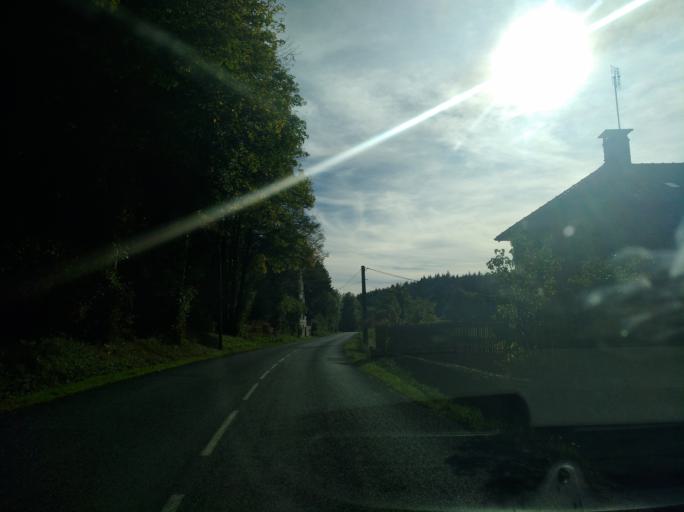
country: FR
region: Rhone-Alpes
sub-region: Departement de la Loire
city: Belmont-de-la-Loire
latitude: 46.1704
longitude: 4.4424
